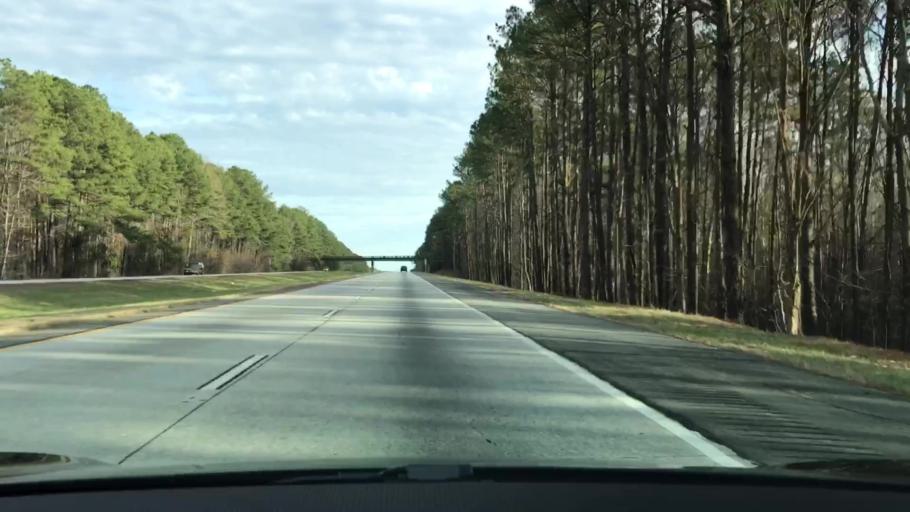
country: US
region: Georgia
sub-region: Taliaferro County
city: Crawfordville
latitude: 33.5132
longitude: -82.8510
